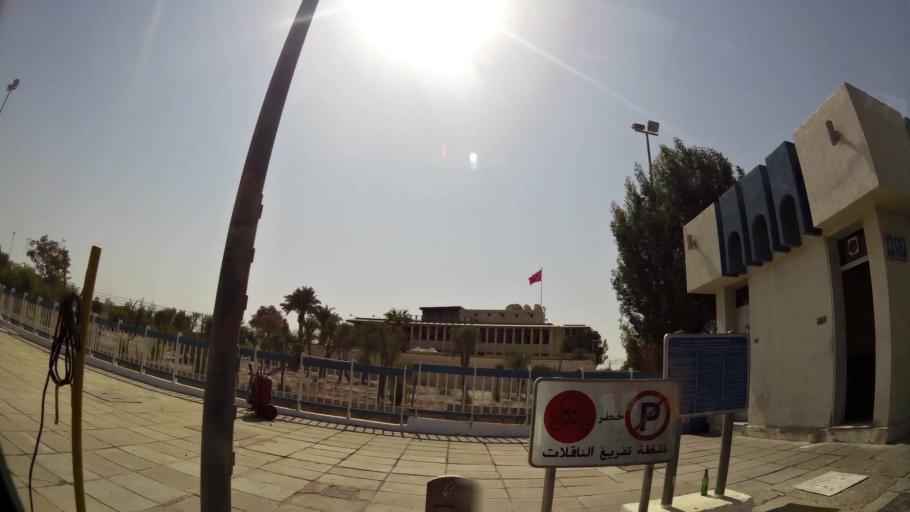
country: KW
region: Al Asimah
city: Ad Dasmah
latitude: 29.3673
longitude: 48.0163
